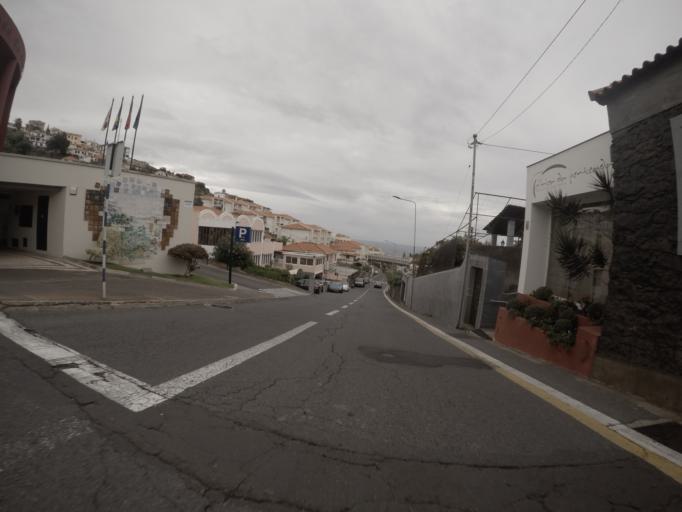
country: PT
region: Madeira
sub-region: Funchal
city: Nossa Senhora do Monte
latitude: 32.6632
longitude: -16.9290
